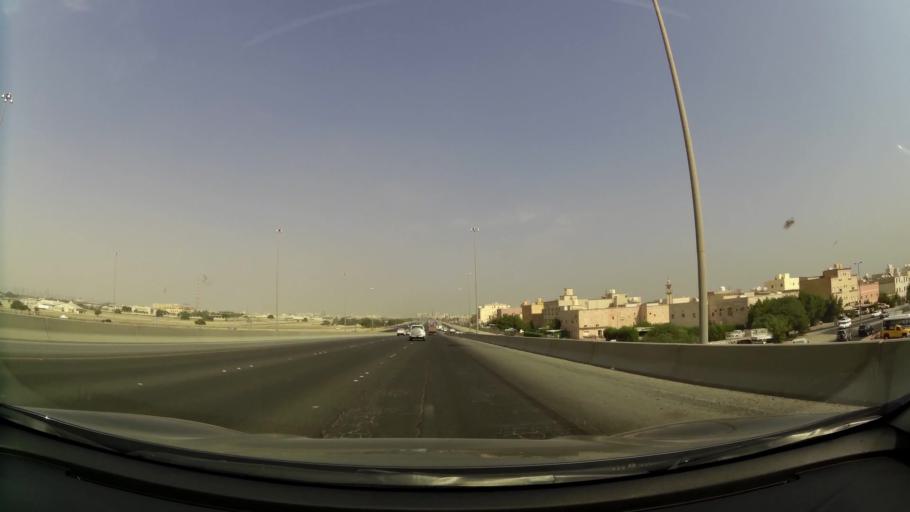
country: KW
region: Al Ahmadi
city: Al Fahahil
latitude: 29.0746
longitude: 48.1122
